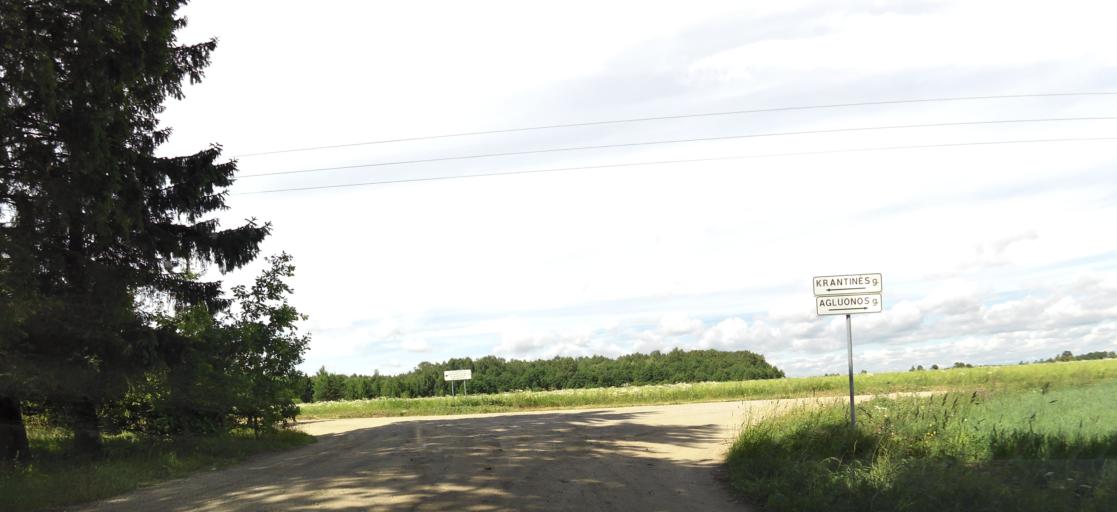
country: LT
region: Panevezys
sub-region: Birzai
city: Birzai
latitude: 56.1781
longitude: 24.7477
